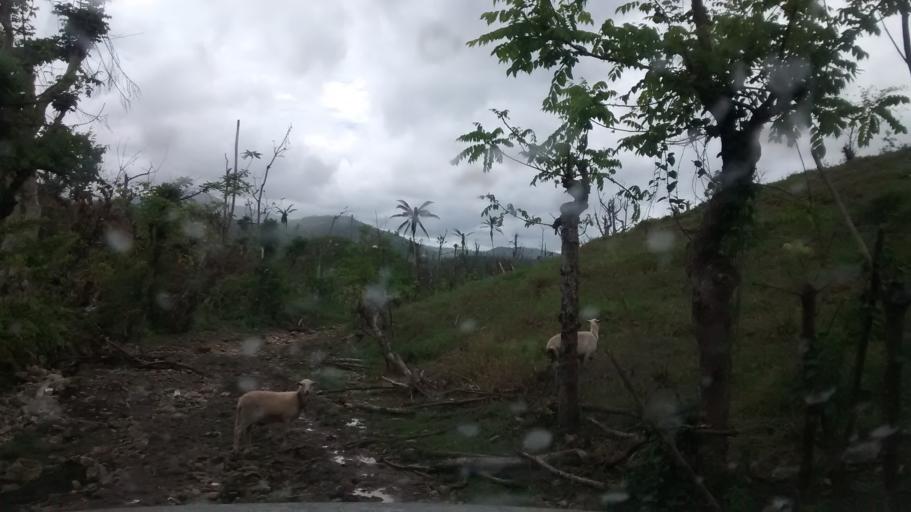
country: HT
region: Grandans
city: Moron
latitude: 18.5533
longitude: -74.2685
